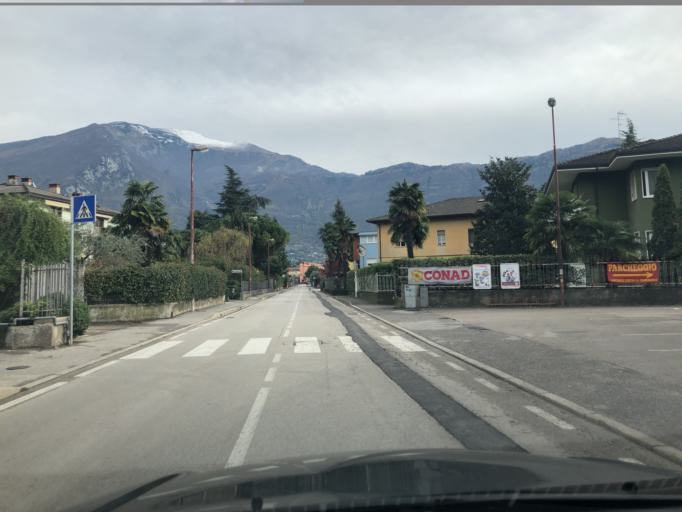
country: IT
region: Trentino-Alto Adige
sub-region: Provincia di Trento
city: Arco
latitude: 45.9174
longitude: 10.8706
